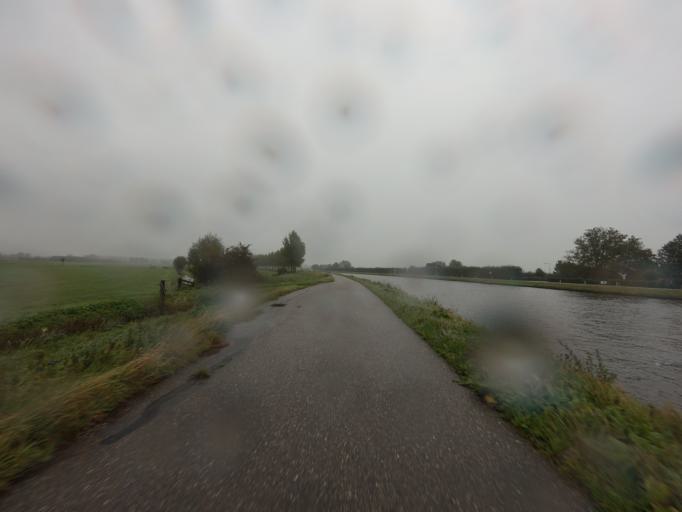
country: NL
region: South Holland
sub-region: Gemeente Leerdam
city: Leerdam
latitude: 51.9388
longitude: 5.0418
